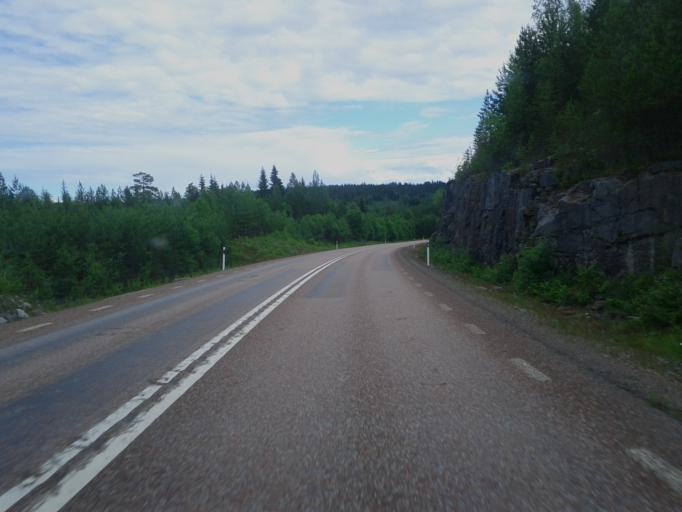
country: SE
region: Dalarna
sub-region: Faluns Kommun
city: Bjursas
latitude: 60.7834
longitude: 15.3091
